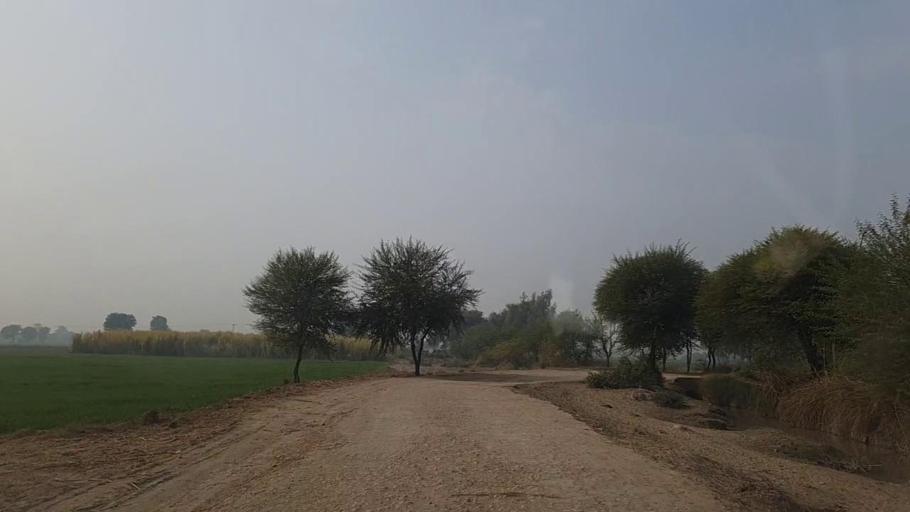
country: PK
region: Sindh
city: Sanghar
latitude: 26.0989
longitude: 68.8973
